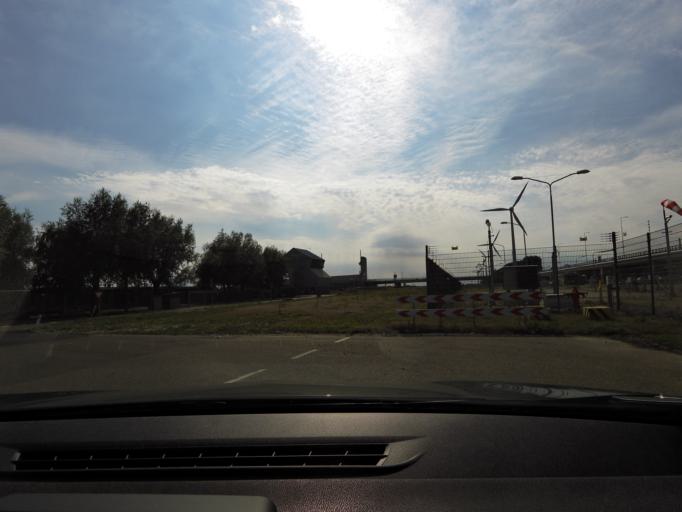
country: NL
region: South Holland
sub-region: Gemeente Spijkenisse
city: Spijkenisse
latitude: 51.8677
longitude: 4.3118
